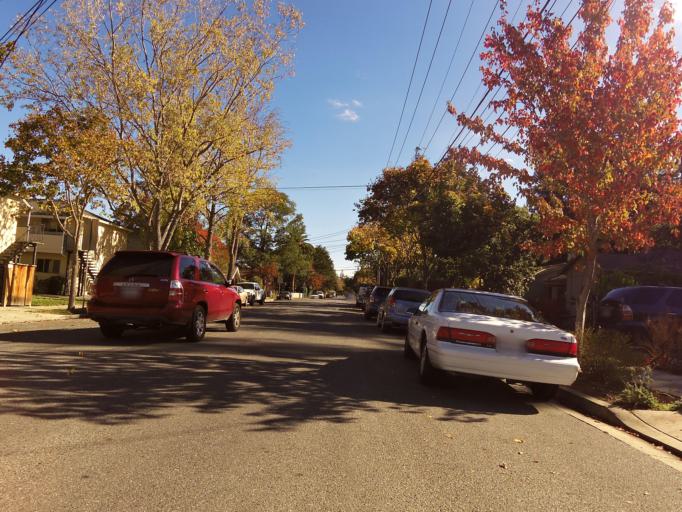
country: US
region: California
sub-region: Santa Clara County
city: Mountain View
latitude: 37.3927
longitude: -122.0920
